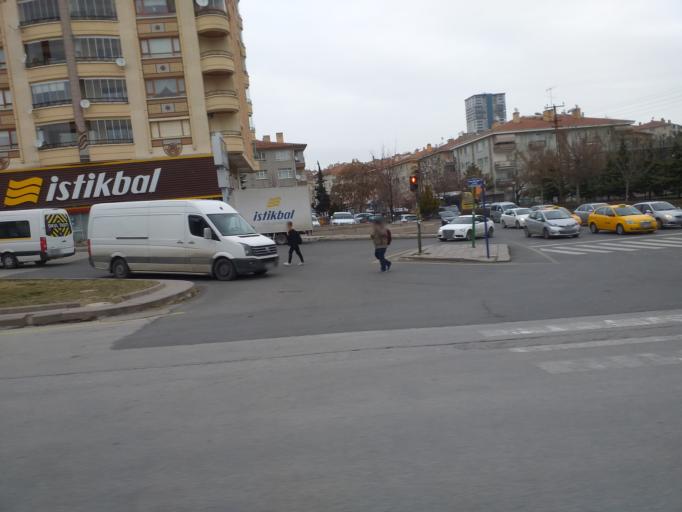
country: TR
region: Ankara
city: Ankara
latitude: 39.9690
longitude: 32.8315
